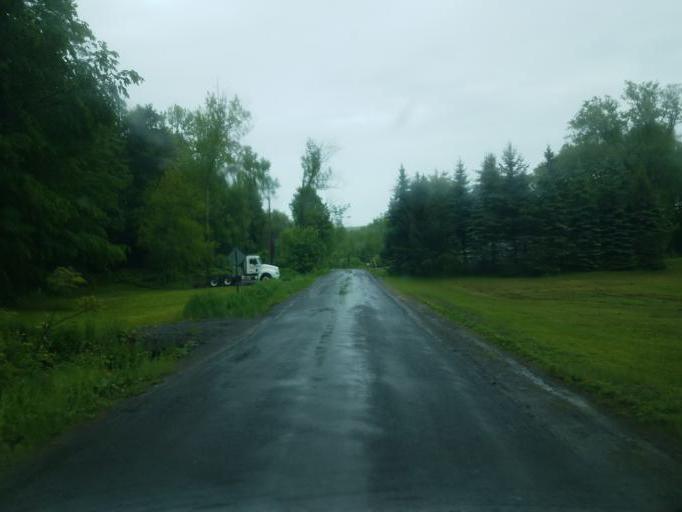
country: US
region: New York
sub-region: Herkimer County
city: Ilion
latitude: 42.9590
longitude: -75.0317
